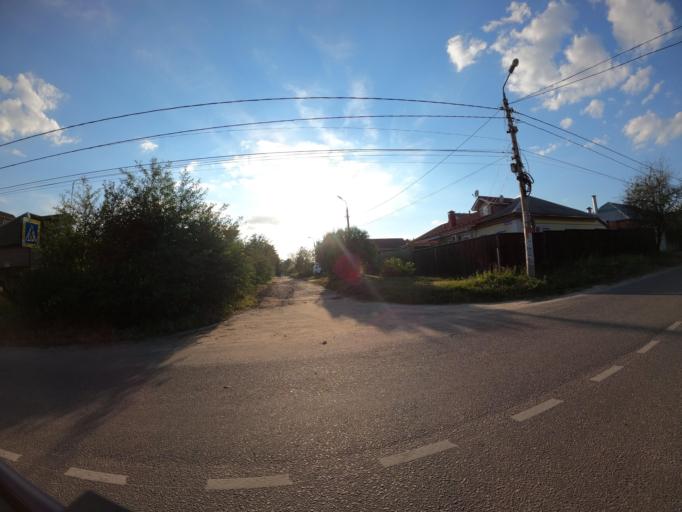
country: RU
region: Moskovskaya
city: Raduzhnyy
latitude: 55.1054
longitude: 38.7274
